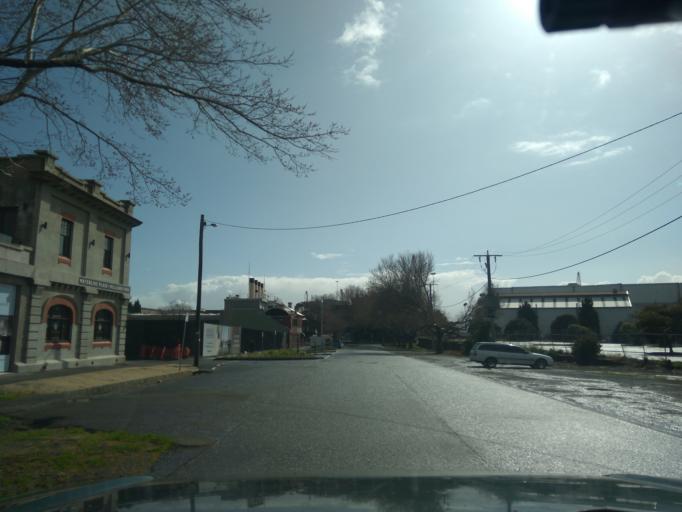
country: AU
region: Victoria
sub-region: Hobsons Bay
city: Williamstown
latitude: -37.8663
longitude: 144.9096
